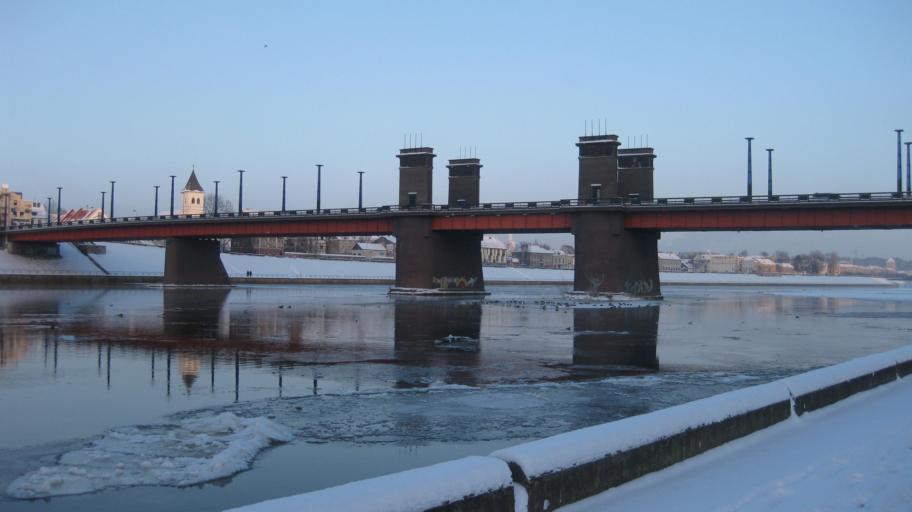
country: LT
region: Kauno apskritis
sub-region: Kaunas
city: Kaunas
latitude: 54.8948
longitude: 23.8878
